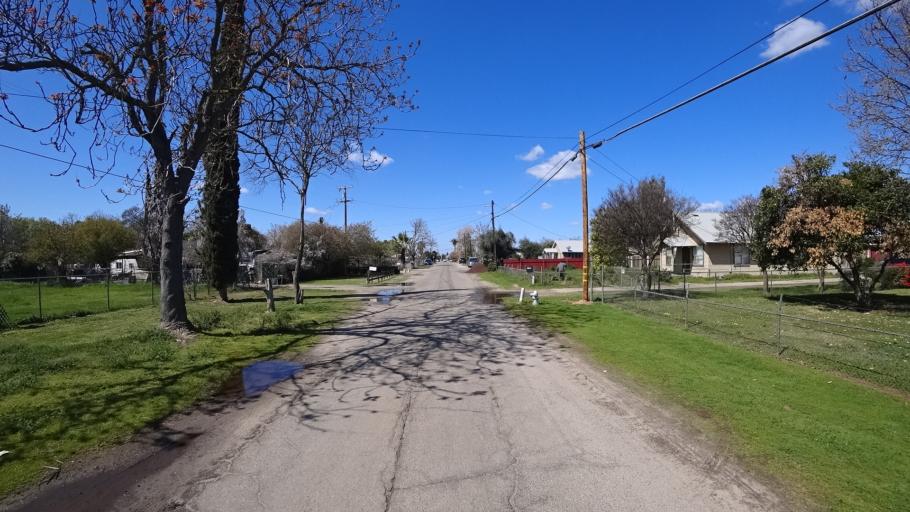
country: US
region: California
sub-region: Fresno County
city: West Park
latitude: 36.8098
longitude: -119.8834
